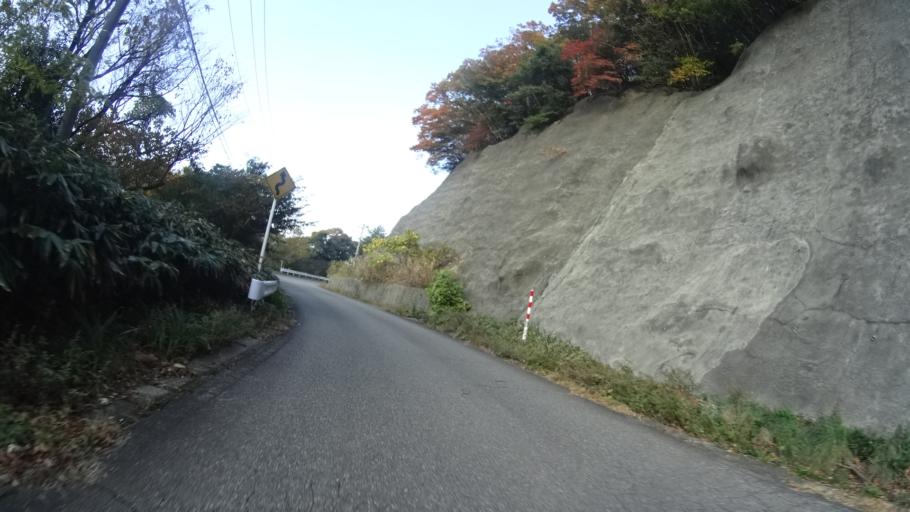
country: JP
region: Ishikawa
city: Nanao
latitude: 37.0131
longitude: 136.9873
